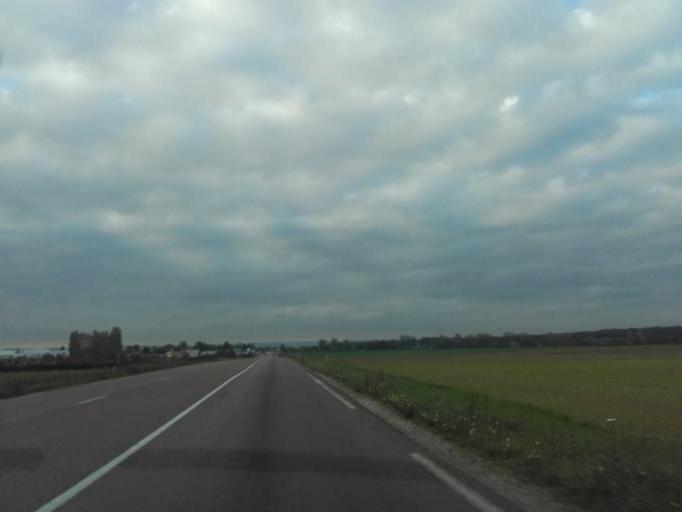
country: FR
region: Bourgogne
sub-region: Departement de Saone-et-Loire
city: Champforgeuil
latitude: 46.8374
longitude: 4.8185
